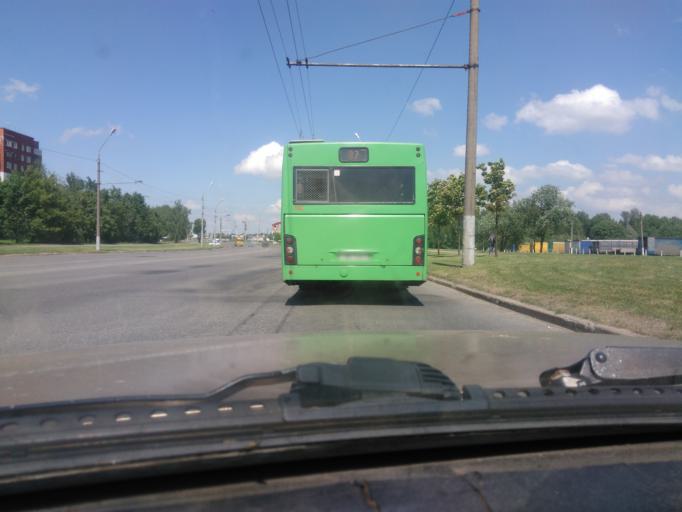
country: BY
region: Mogilev
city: Palykavichy Pyershyya
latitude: 53.9564
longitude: 30.3639
